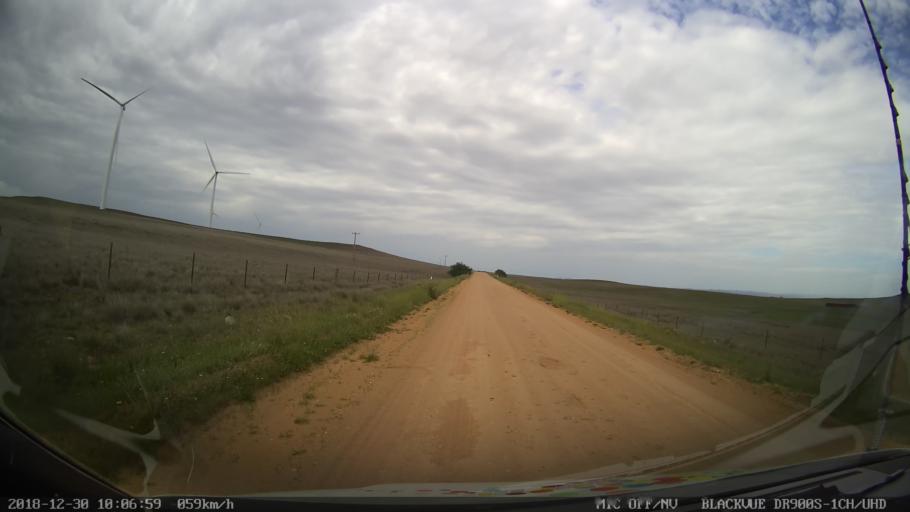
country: AU
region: New South Wales
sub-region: Cooma-Monaro
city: Cooma
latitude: -36.5363
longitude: 149.1259
